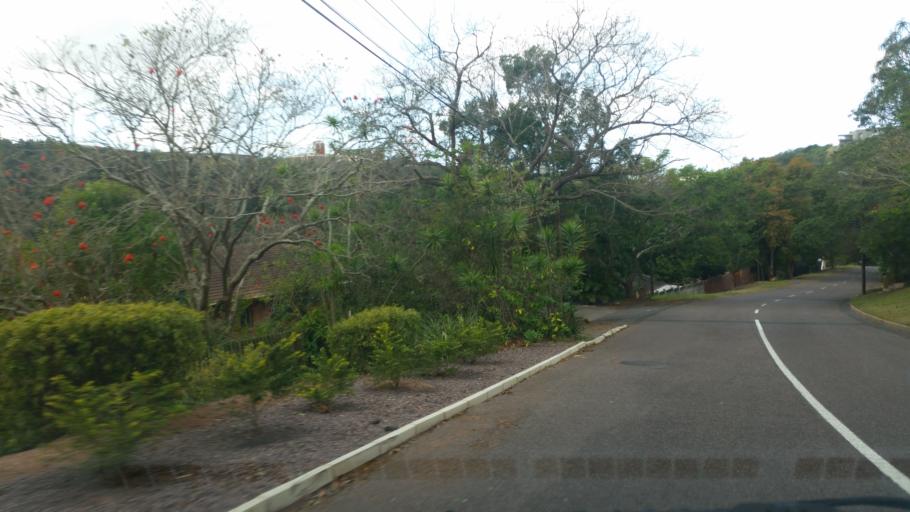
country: ZA
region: KwaZulu-Natal
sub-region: eThekwini Metropolitan Municipality
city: Berea
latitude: -29.8211
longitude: 30.9354
